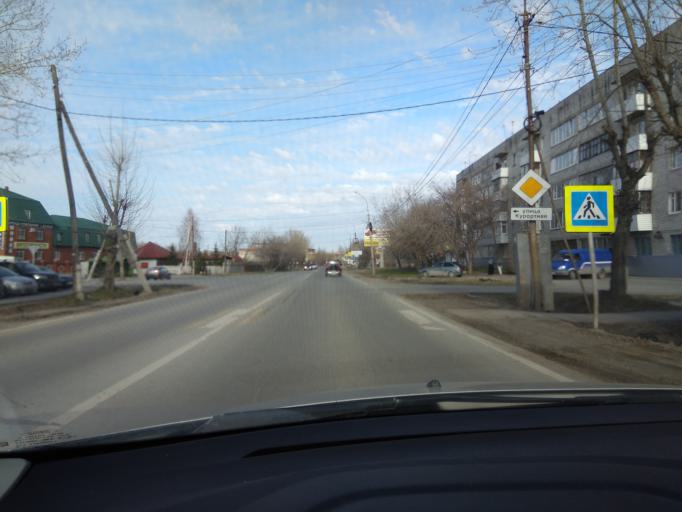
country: RU
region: Tjumen
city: Moskovskiy
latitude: 57.1564
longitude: 65.4473
